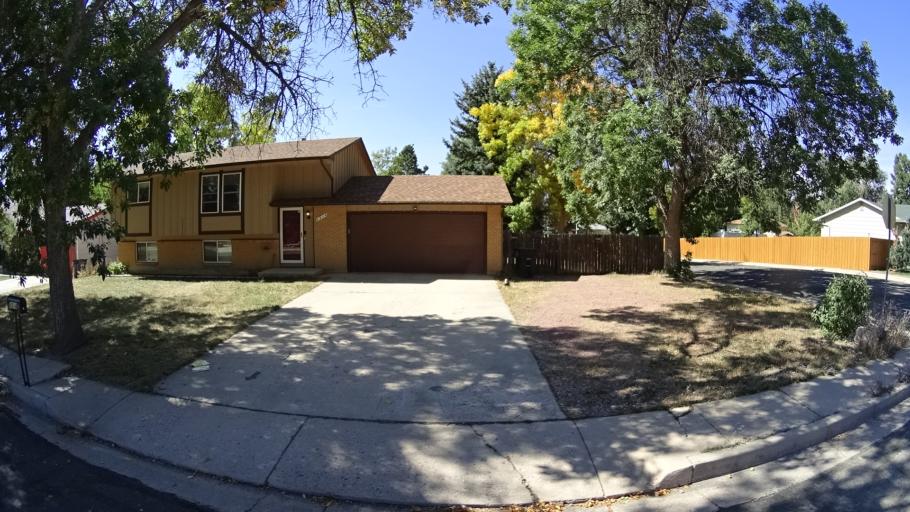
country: US
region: Colorado
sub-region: El Paso County
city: Cimarron Hills
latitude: 38.9039
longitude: -104.7617
